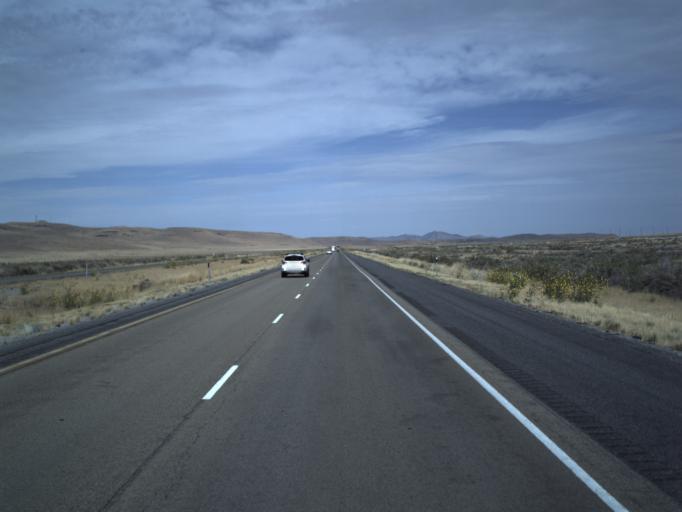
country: US
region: Utah
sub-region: Tooele County
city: Grantsville
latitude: 40.7827
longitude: -112.8173
